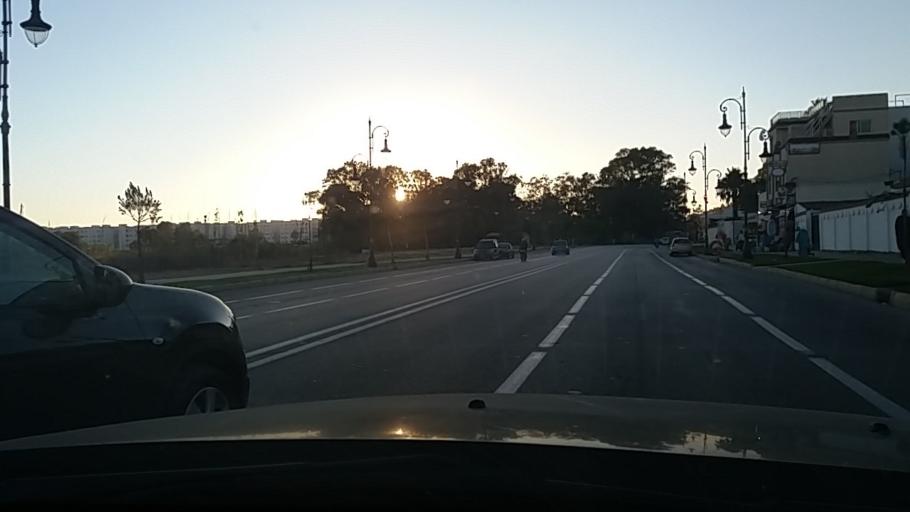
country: MA
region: Tanger-Tetouan
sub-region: Tanger-Assilah
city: Boukhalef
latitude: 35.7407
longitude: -5.8787
